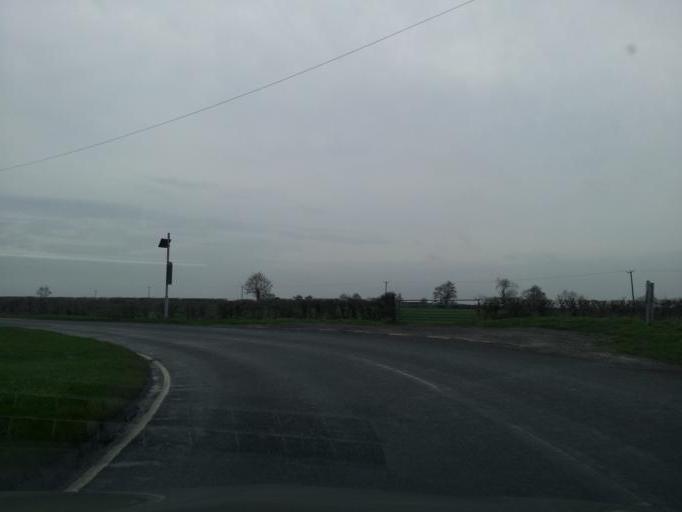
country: GB
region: England
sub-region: Lincolnshire
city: Long Bennington
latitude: 52.9544
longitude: -0.7965
